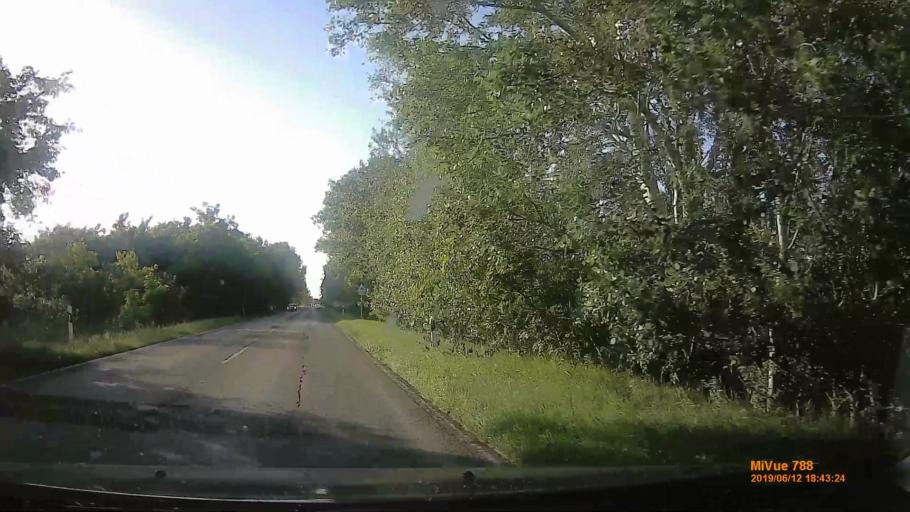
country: HU
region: Csongrad
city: Pusztaszer
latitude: 46.5515
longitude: 19.9495
